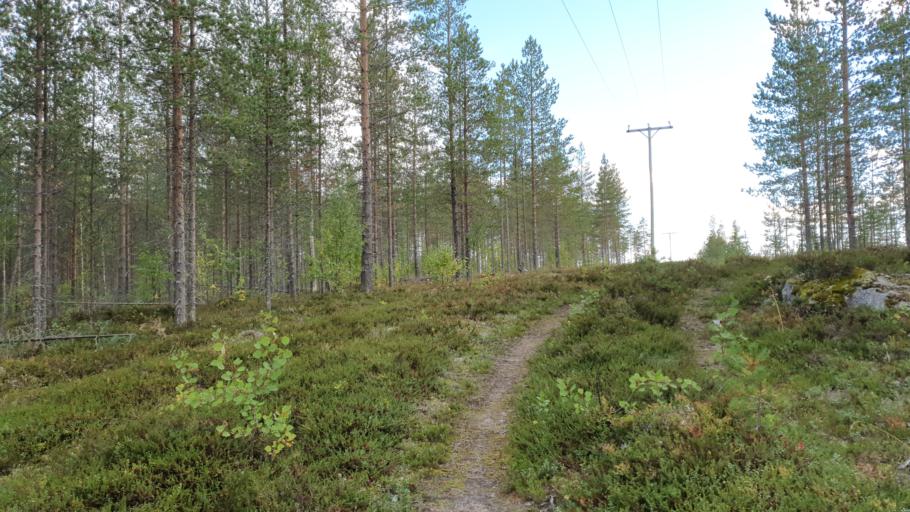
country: FI
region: Kainuu
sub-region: Kehys-Kainuu
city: Kuhmo
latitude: 64.2001
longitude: 29.1603
